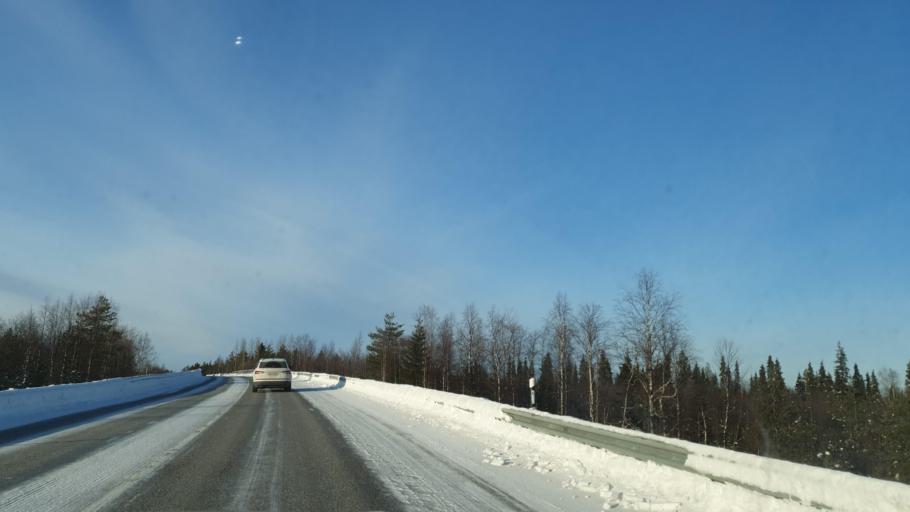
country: FI
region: Lapland
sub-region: Tunturi-Lappi
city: Kolari
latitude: 67.3067
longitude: 23.8323
